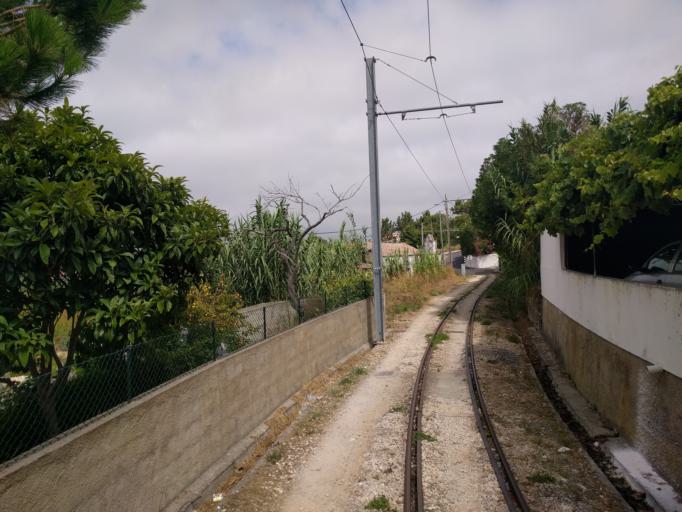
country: PT
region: Lisbon
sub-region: Sintra
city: Colares
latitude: 38.8022
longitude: -9.4447
